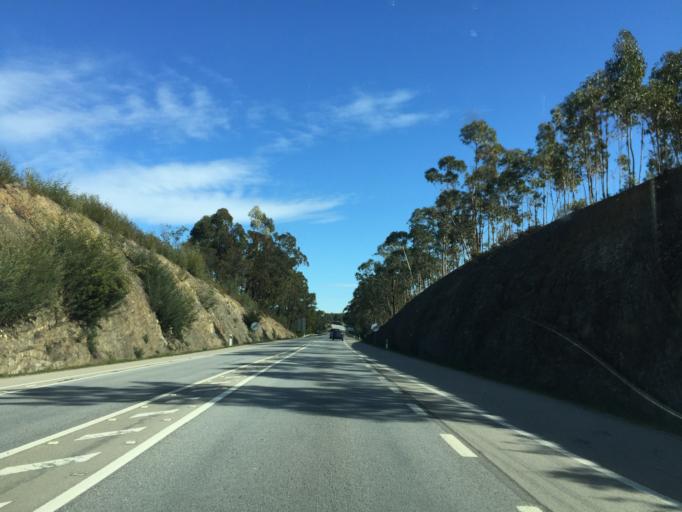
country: PT
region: Castelo Branco
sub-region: Castelo Branco
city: Castelo Branco
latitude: 39.7926
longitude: -7.5509
